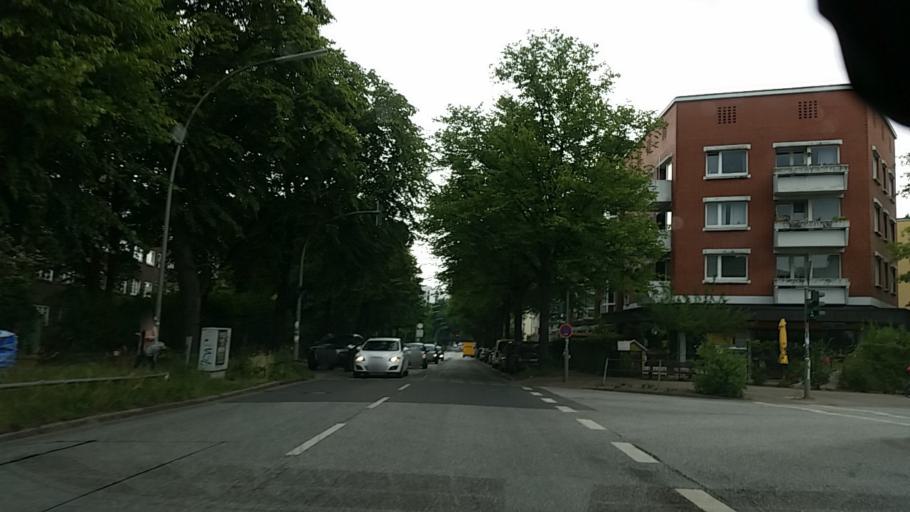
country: DE
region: Hamburg
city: Altona
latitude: 53.5583
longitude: 9.9140
